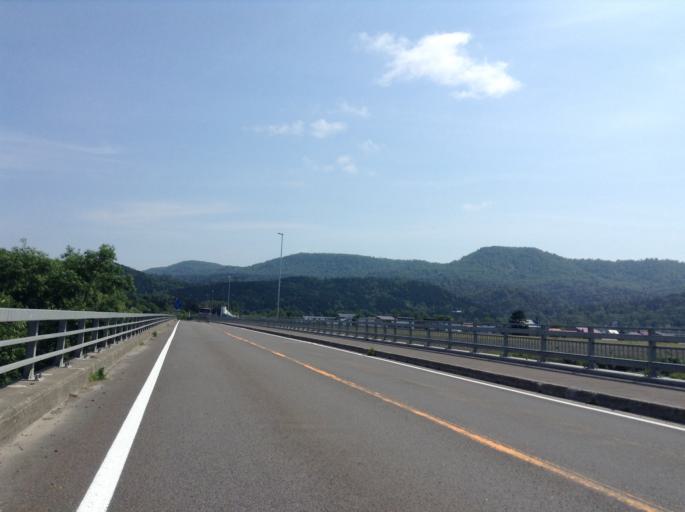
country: JP
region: Hokkaido
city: Nayoro
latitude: 44.7263
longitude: 142.2539
